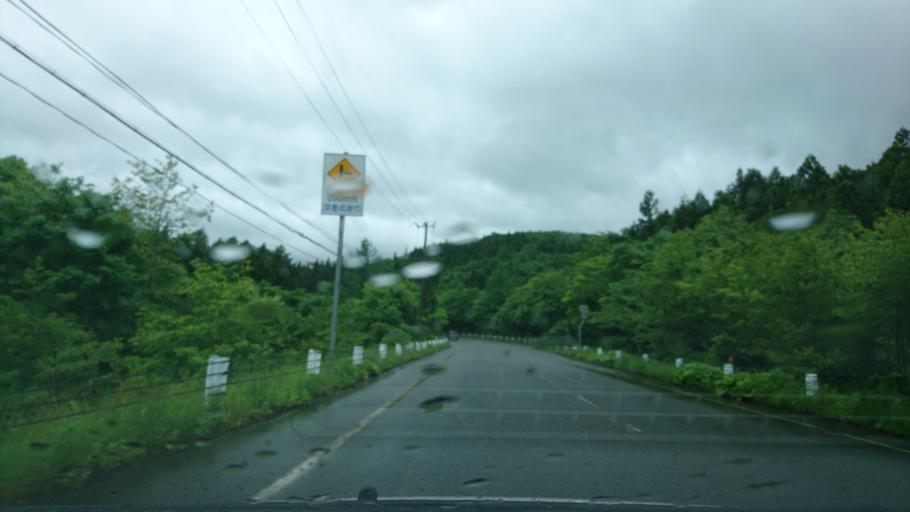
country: JP
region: Iwate
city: Ichinoseki
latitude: 39.0131
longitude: 140.8676
